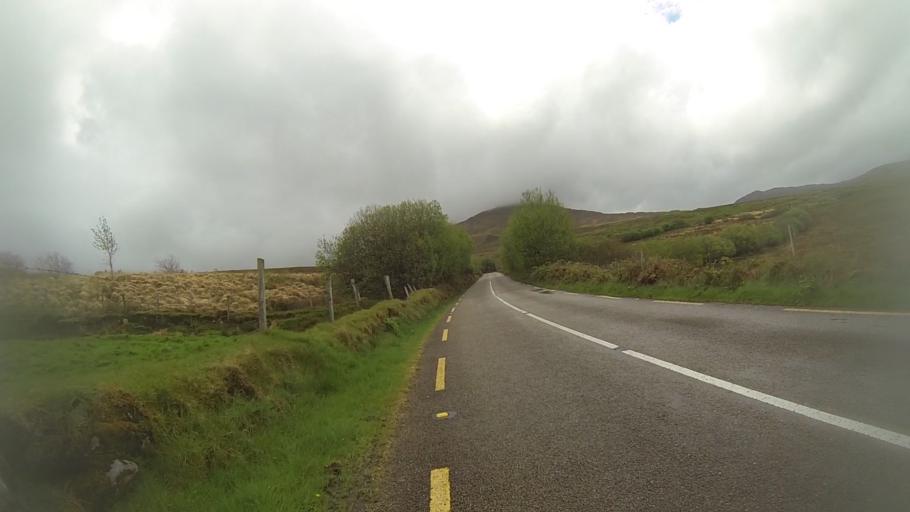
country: IE
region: Munster
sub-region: Ciarrai
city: Kenmare
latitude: 51.8825
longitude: -9.7866
